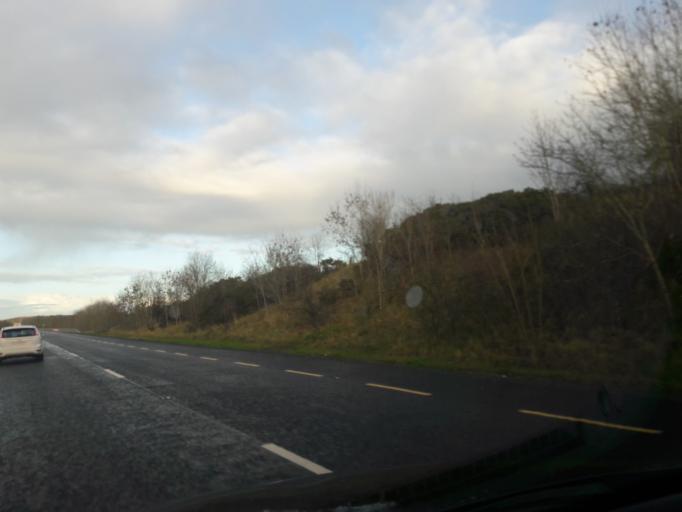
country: IE
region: Ulster
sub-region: County Monaghan
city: Carrickmacross
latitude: 54.0018
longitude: -6.7152
